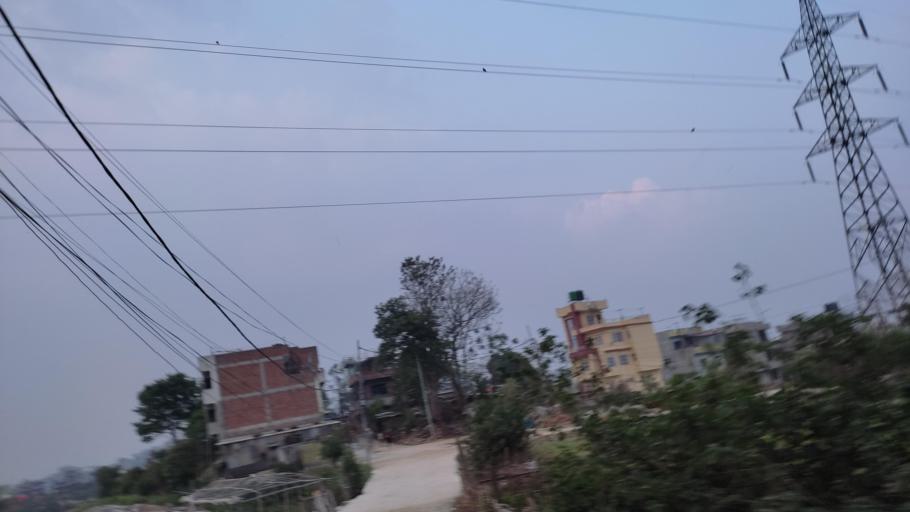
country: NP
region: Central Region
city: Kirtipur
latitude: 27.6708
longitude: 85.2644
